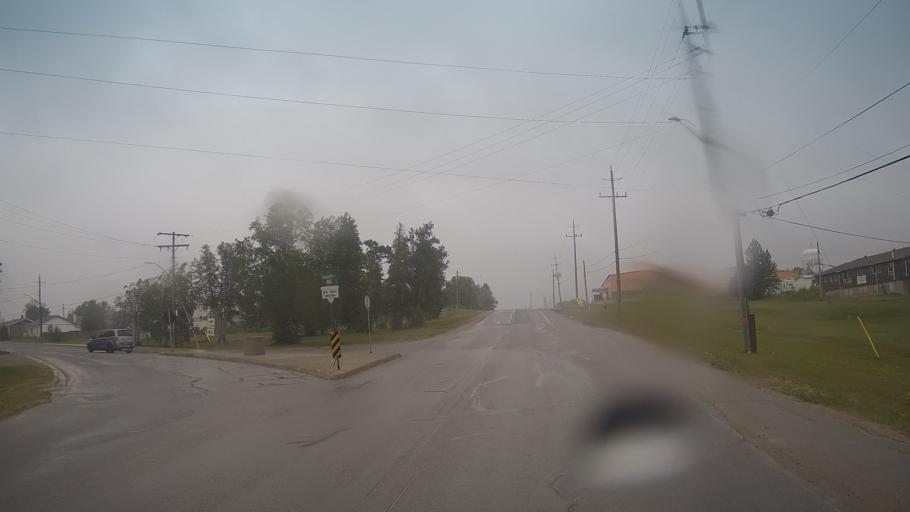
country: CA
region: Ontario
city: Greenstone
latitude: 49.7758
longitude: -86.5364
